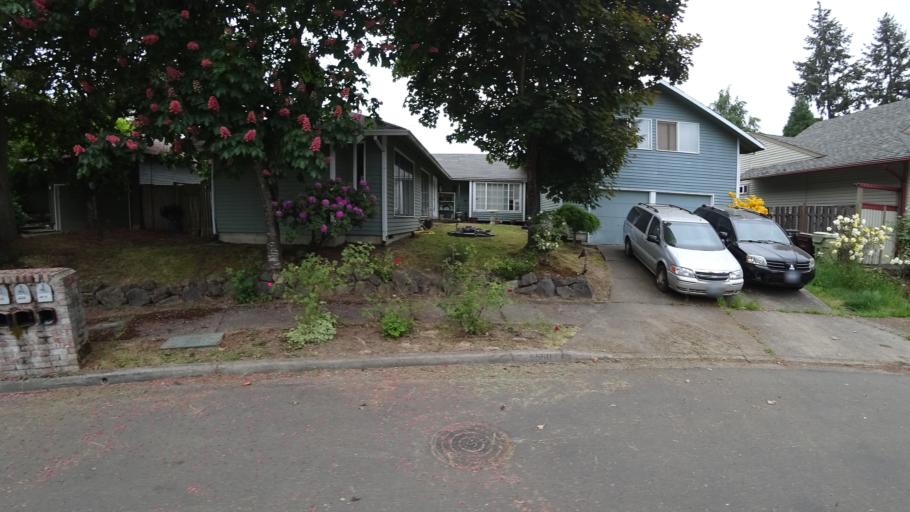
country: US
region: Oregon
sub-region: Washington County
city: Rockcreek
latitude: 45.5598
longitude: -122.8829
